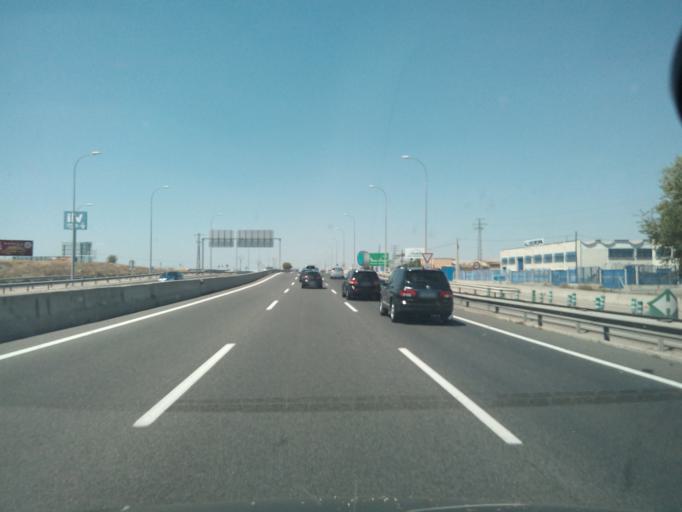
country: ES
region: Madrid
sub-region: Provincia de Madrid
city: Ciempozuelos
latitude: 40.1429
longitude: -3.6582
